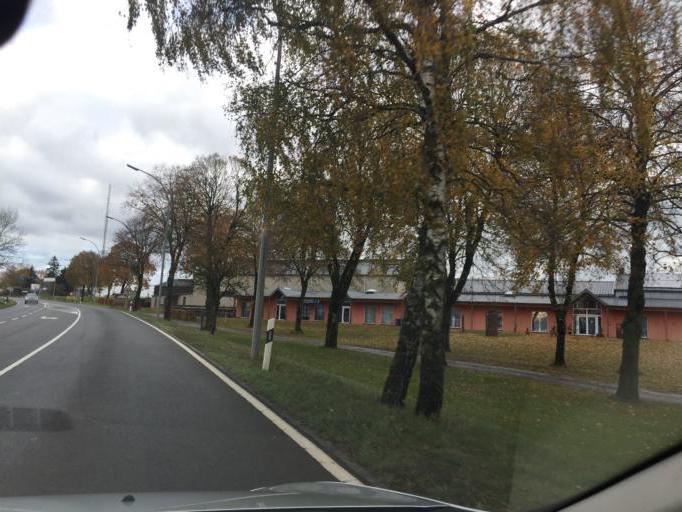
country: LU
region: Diekirch
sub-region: Canton de Wiltz
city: Goesdorf
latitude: 49.8845
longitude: 5.9847
